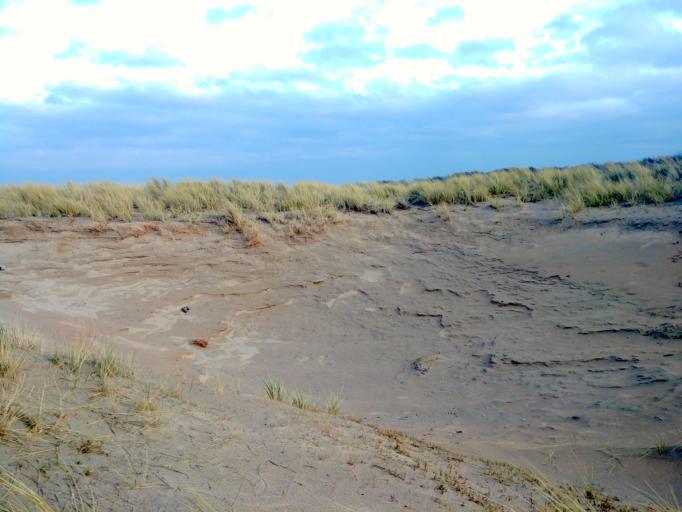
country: NL
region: North Holland
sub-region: Gemeente Zandvoort
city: Zandvoort
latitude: 52.3329
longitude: 4.4982
